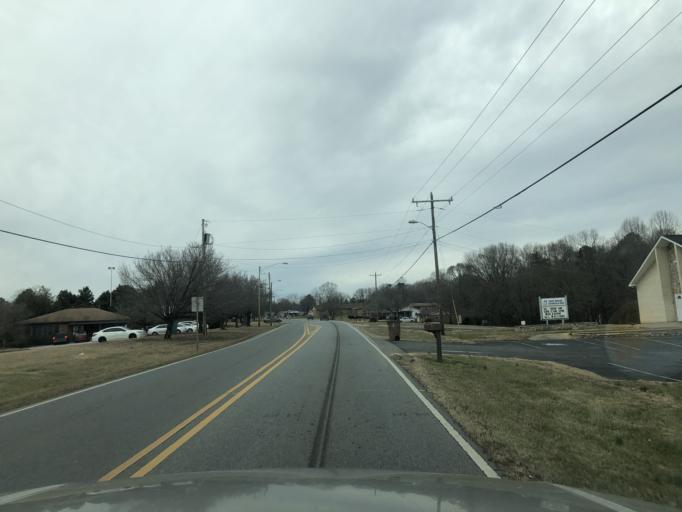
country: US
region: North Carolina
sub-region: Cleveland County
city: Shelby
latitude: 35.2697
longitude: -81.4802
